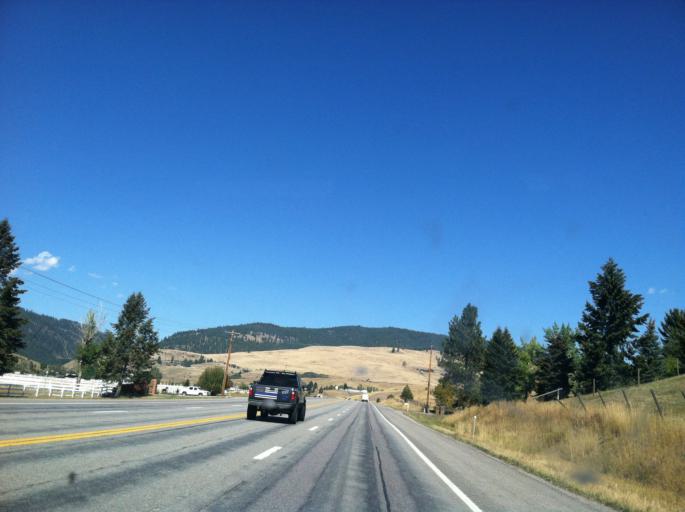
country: US
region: Montana
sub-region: Missoula County
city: Frenchtown
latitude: 46.9736
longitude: -114.1279
